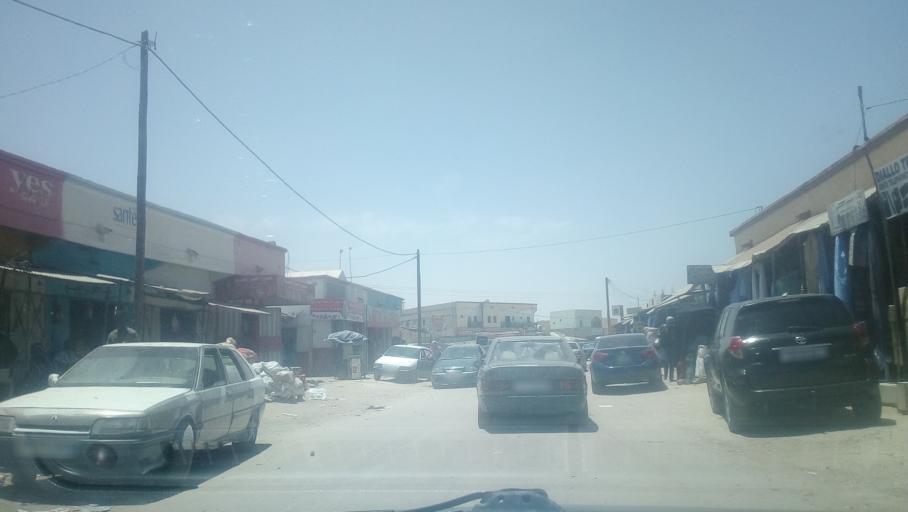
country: MR
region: Nouakchott
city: Nouakchott
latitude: 18.0564
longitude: -15.9616
